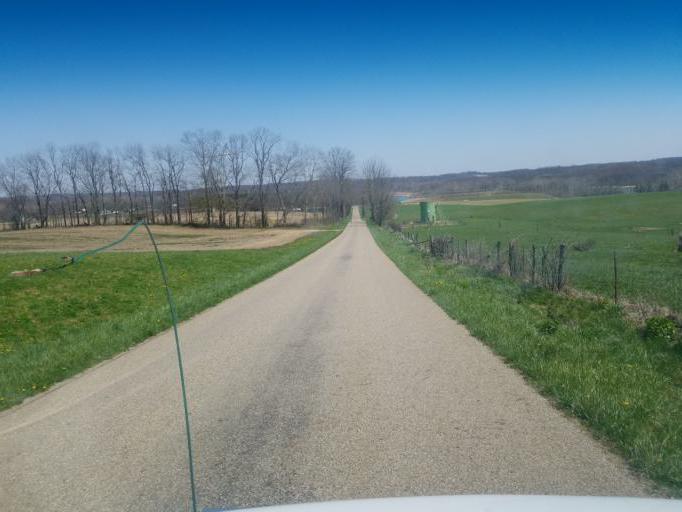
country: US
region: Ohio
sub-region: Knox County
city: Gambier
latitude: 40.3876
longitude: -82.3611
